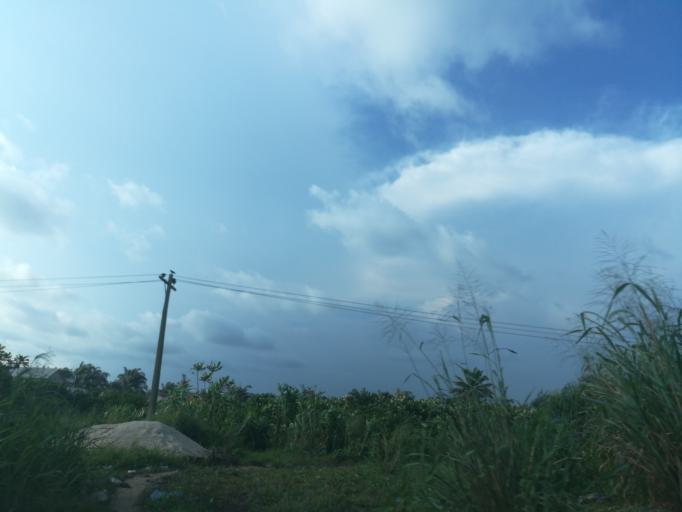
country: NG
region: Ogun
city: Ado Odo
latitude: 6.4863
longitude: 3.0614
